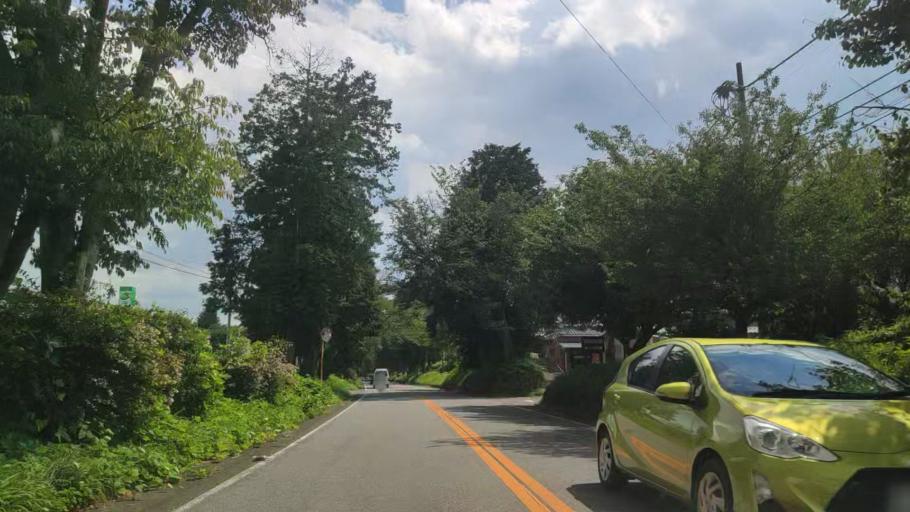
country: JP
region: Tochigi
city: Utsunomiya-shi
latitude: 36.6163
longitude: 139.8536
